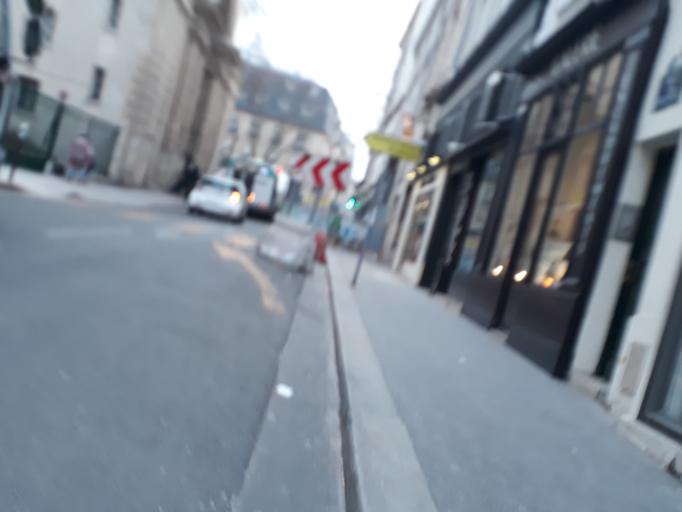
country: FR
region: Ile-de-France
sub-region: Paris
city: Paris
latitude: 48.8552
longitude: 2.3309
